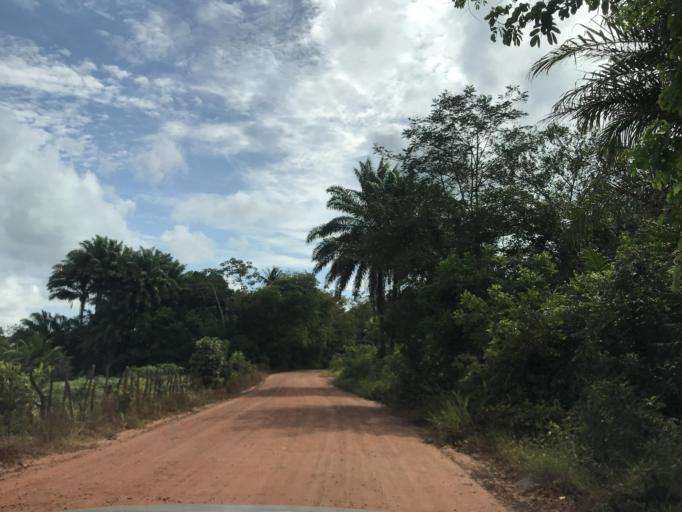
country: BR
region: Bahia
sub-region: Entre Rios
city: Entre Rios
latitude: -12.1722
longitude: -38.1420
